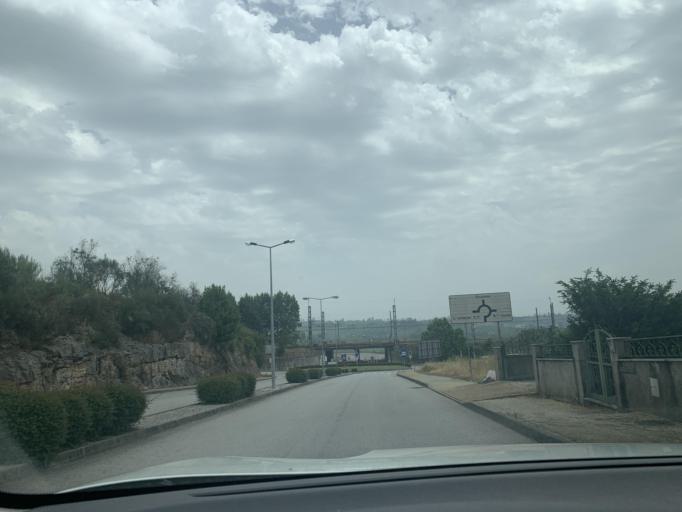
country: PT
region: Viseu
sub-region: Mangualde
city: Mangualde
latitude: 40.5867
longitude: -7.7640
